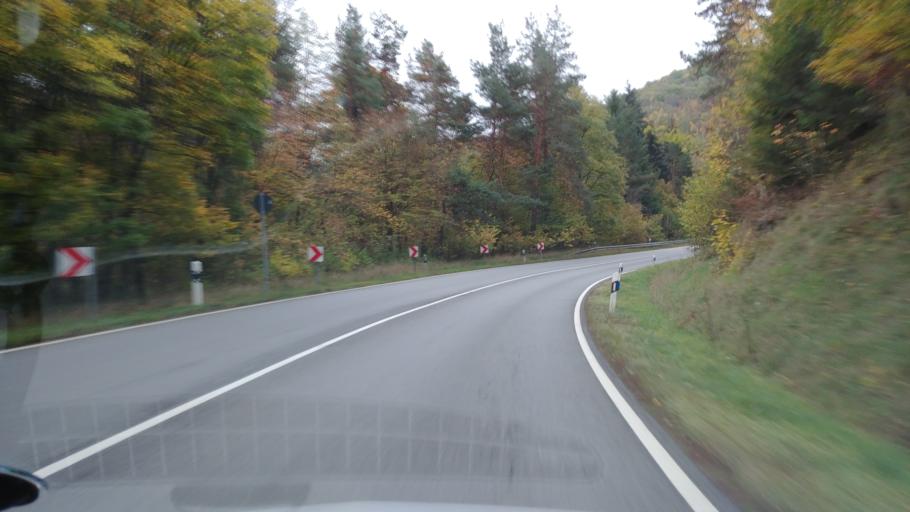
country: DE
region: Hesse
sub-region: Regierungsbezirk Darmstadt
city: Idstein
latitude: 50.2288
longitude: 8.2257
